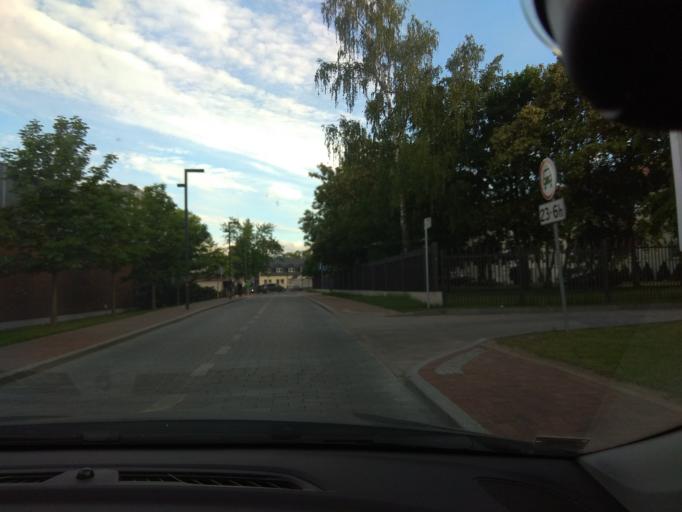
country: LT
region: Marijampoles apskritis
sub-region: Marijampole Municipality
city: Marijampole
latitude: 54.5564
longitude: 23.3451
